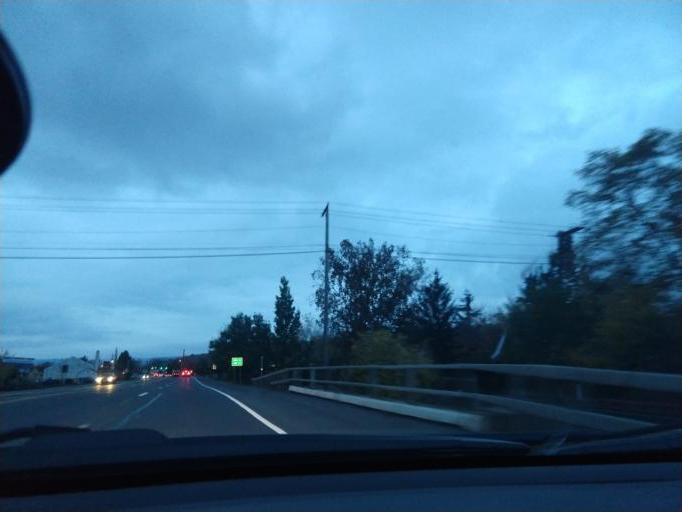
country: US
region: New York
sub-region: Tompkins County
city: Ithaca
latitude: 42.4509
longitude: -76.5042
